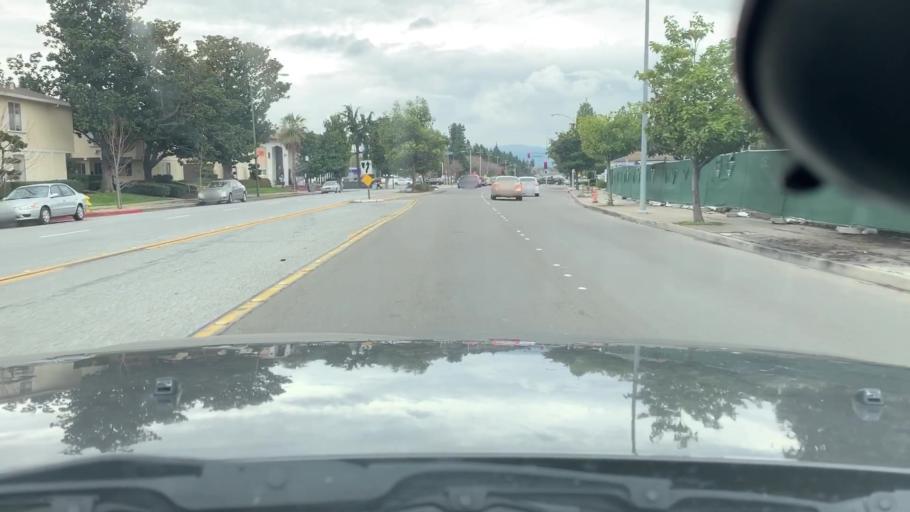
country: US
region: California
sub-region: Santa Clara County
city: Milpitas
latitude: 37.4167
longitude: -121.8734
